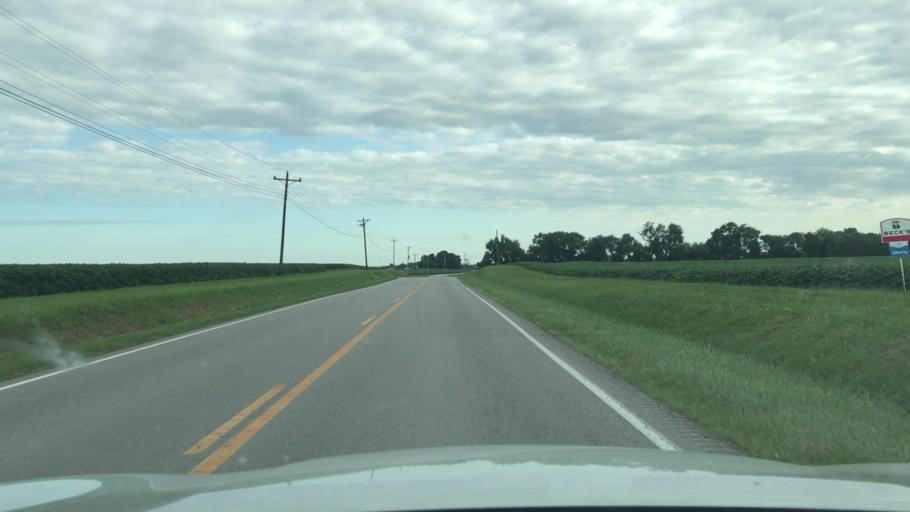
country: US
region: Kentucky
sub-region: Todd County
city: Elkton
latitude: 36.7681
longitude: -87.1668
